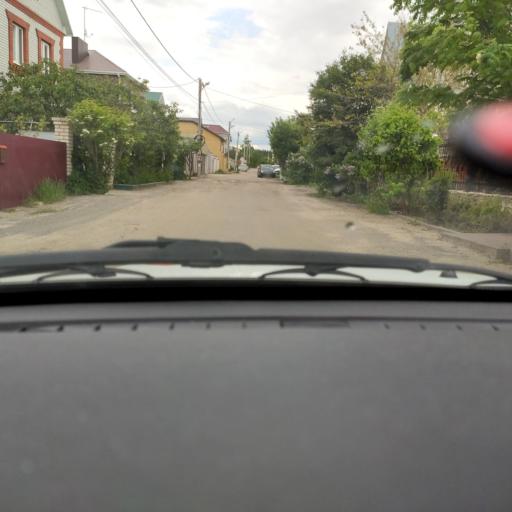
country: RU
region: Voronezj
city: Podgornoye
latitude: 51.7461
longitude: 39.1529
